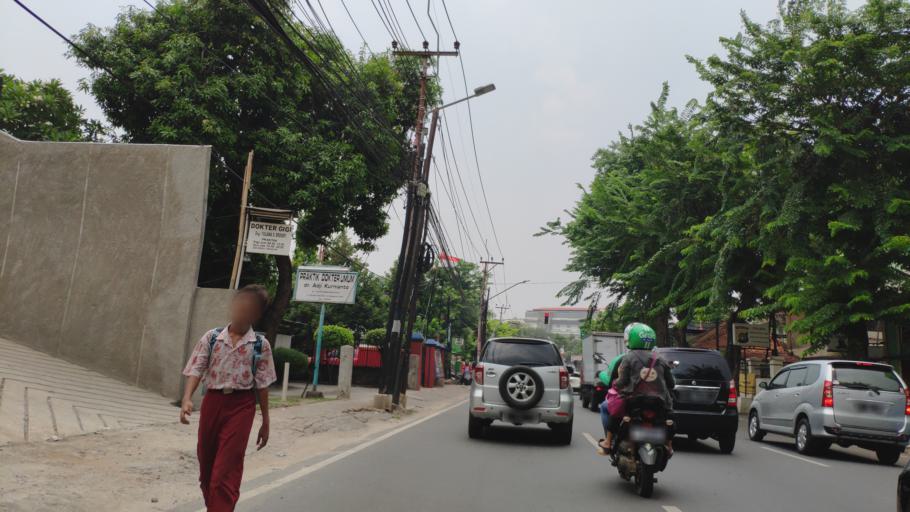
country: ID
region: Banten
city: South Tangerang
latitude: -6.2504
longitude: 106.7782
